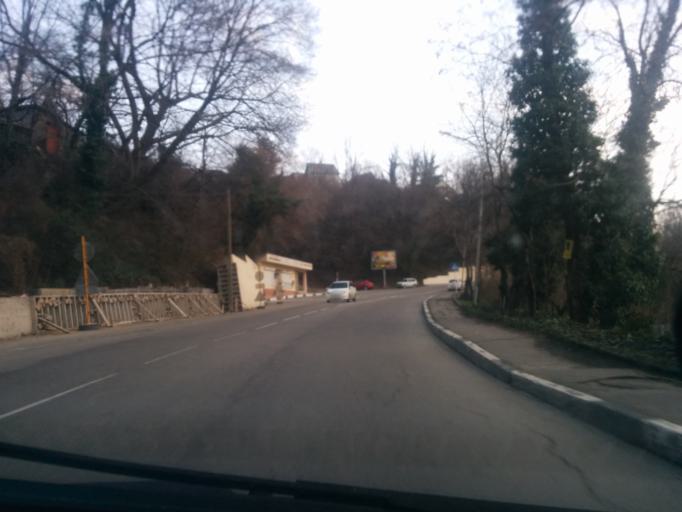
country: RU
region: Krasnodarskiy
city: Tuapse
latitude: 44.1054
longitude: 39.0632
